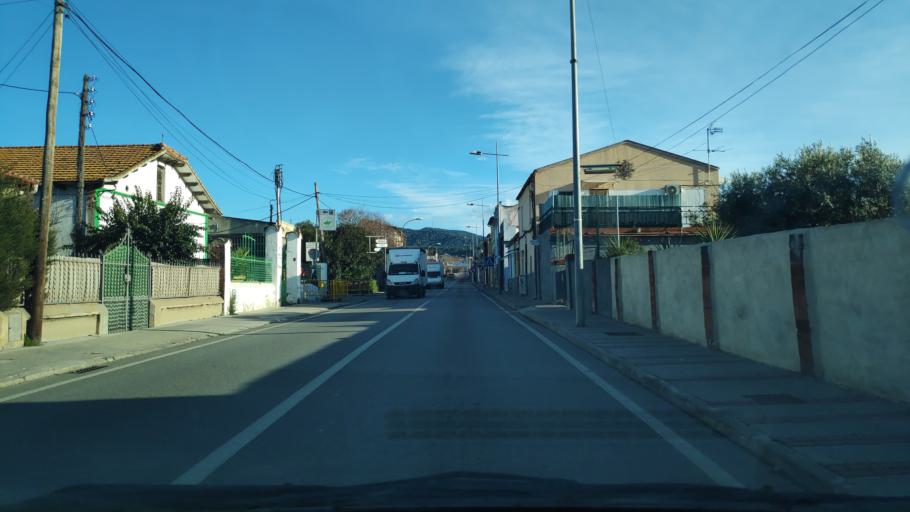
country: ES
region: Catalonia
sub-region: Provincia de Barcelona
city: Mollet del Valles
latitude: 41.5285
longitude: 2.2248
